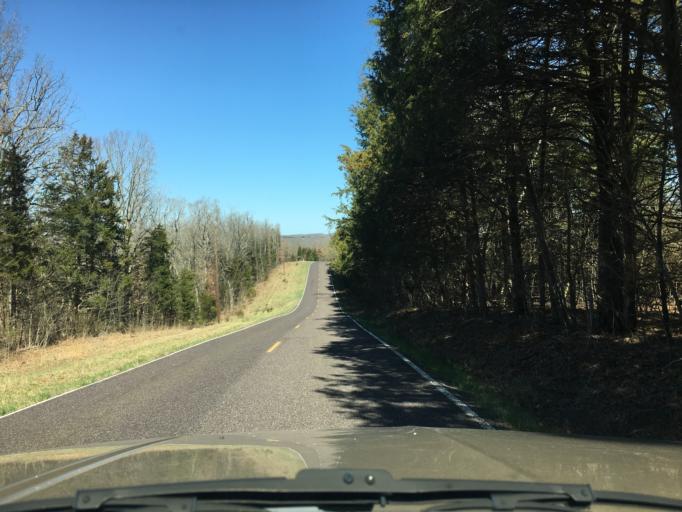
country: US
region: Missouri
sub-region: Franklin County
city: Gerald
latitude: 38.5193
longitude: -91.3273
